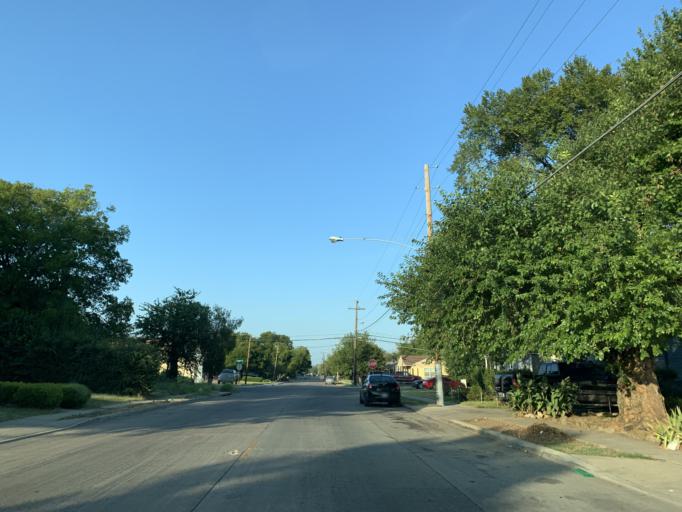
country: US
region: Texas
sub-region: Dallas County
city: Dallas
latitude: 32.7069
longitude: -96.7817
